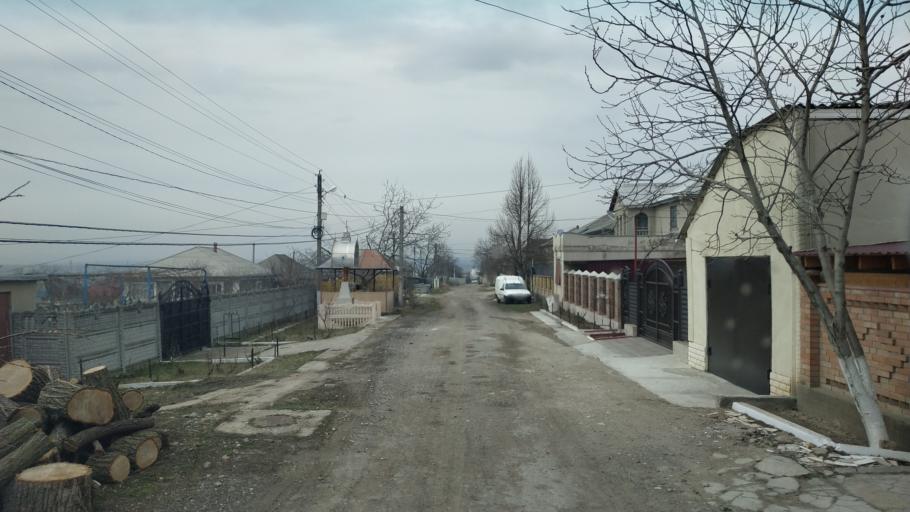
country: MD
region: Chisinau
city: Singera
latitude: 46.9373
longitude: 28.9871
